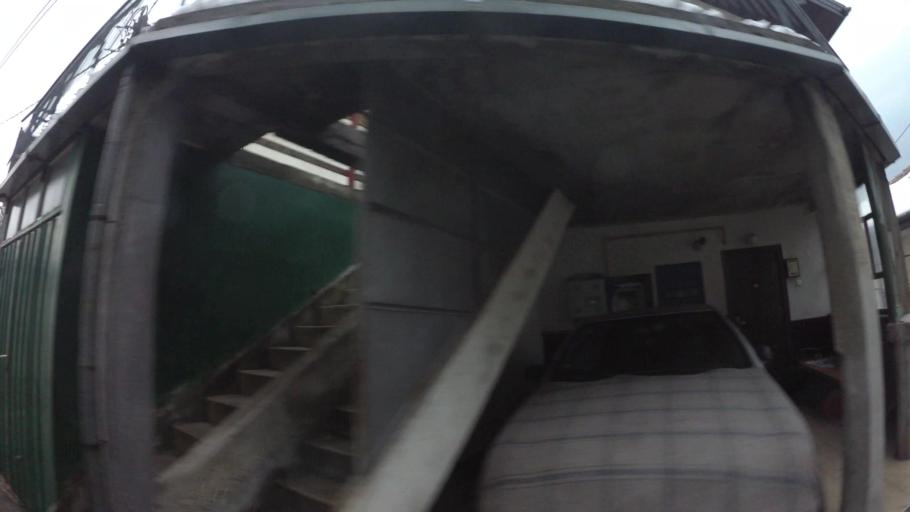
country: BA
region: Federation of Bosnia and Herzegovina
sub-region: Kanton Sarajevo
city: Sarajevo
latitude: 43.8572
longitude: 18.3472
